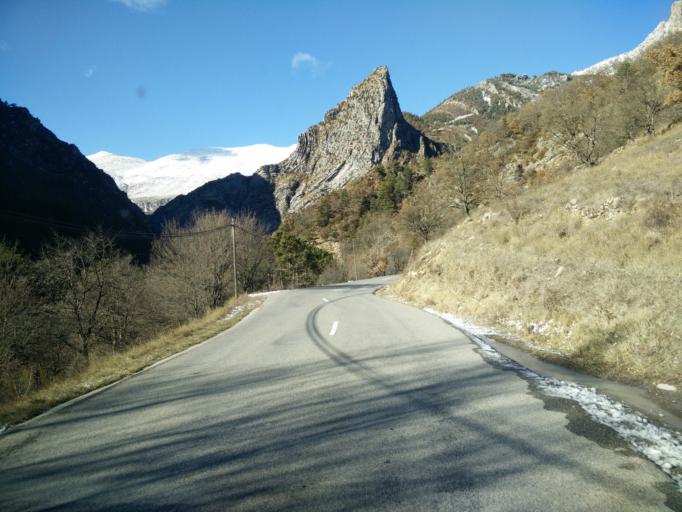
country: FR
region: Provence-Alpes-Cote d'Azur
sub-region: Departement des Alpes-de-Haute-Provence
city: Castellane
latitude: 43.8295
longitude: 6.4579
